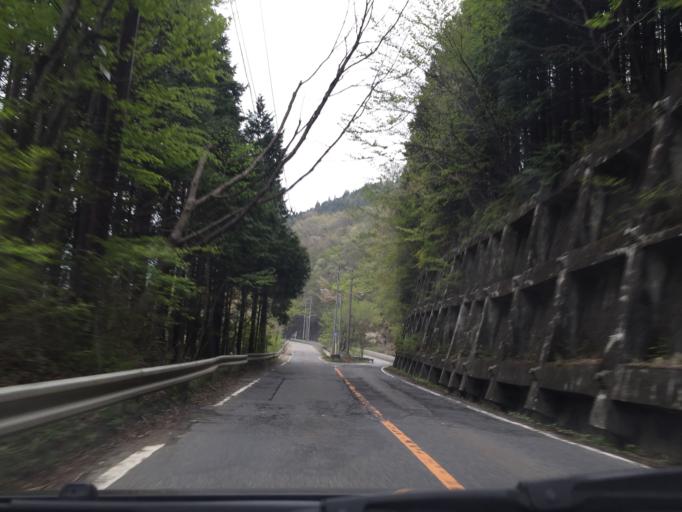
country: JP
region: Tochigi
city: Nikko
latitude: 36.9396
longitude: 139.6970
